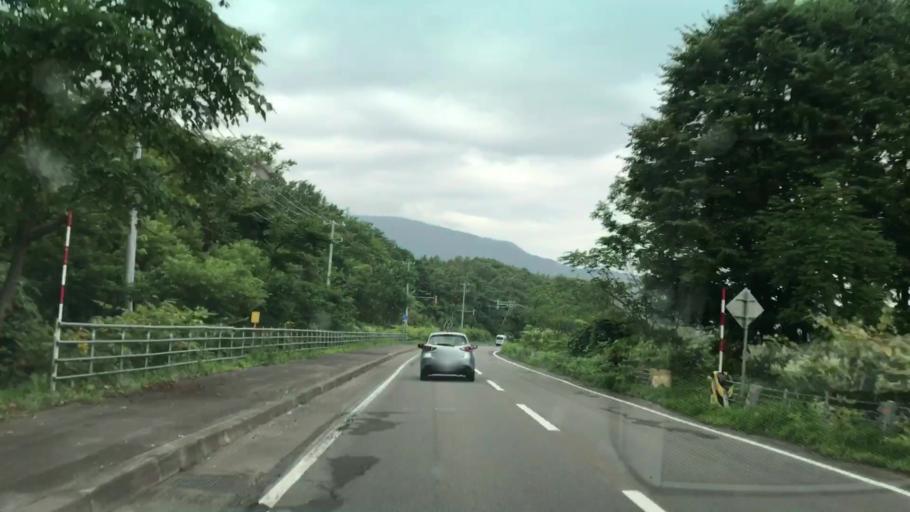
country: JP
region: Hokkaido
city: Iwanai
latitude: 42.7590
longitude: 140.2638
